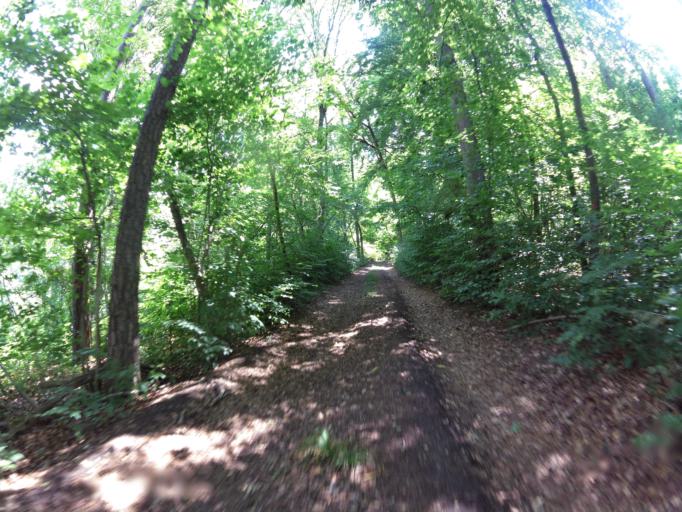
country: DE
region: Bavaria
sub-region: Regierungsbezirk Unterfranken
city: Thungersheim
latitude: 49.8991
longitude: 9.8521
